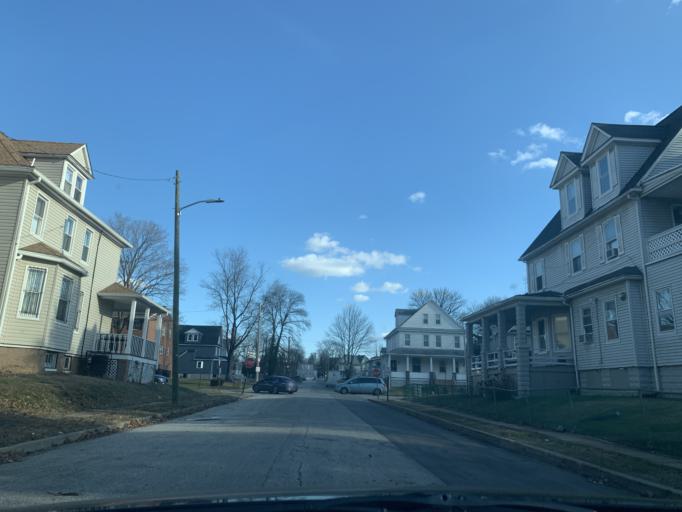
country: US
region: Maryland
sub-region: Baltimore County
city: Lochearn
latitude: 39.3261
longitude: -76.6869
